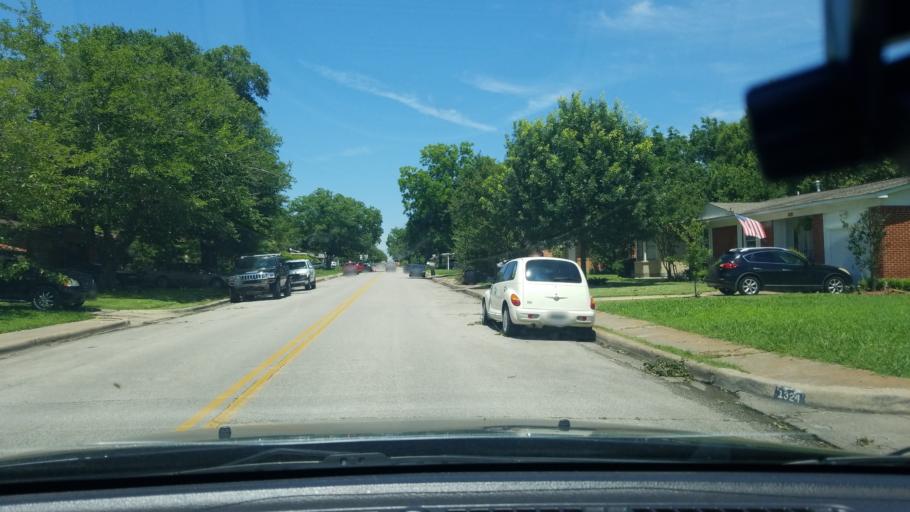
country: US
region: Texas
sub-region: Dallas County
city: Mesquite
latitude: 32.7849
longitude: -96.6178
